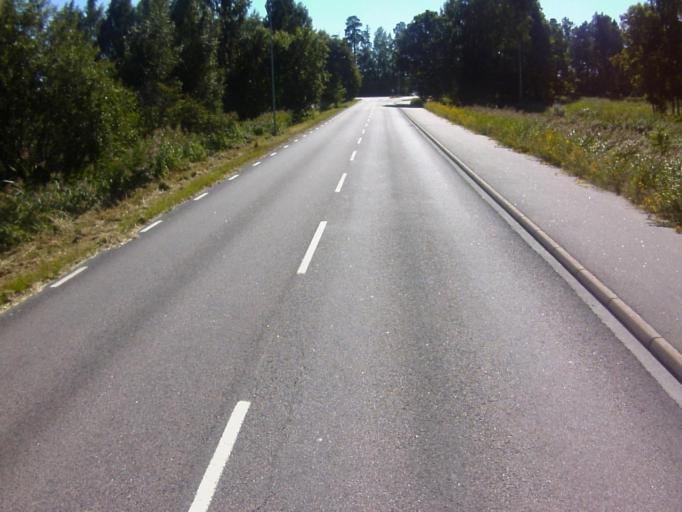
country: SE
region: Soedermanland
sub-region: Eskilstuna Kommun
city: Hallbybrunn
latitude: 59.3815
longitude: 16.4345
